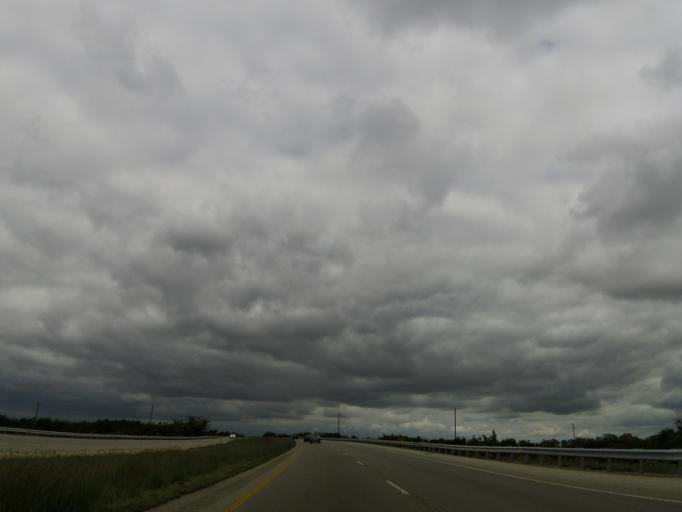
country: US
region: Kentucky
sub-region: Scott County
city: Georgetown
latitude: 38.1864
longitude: -84.5484
